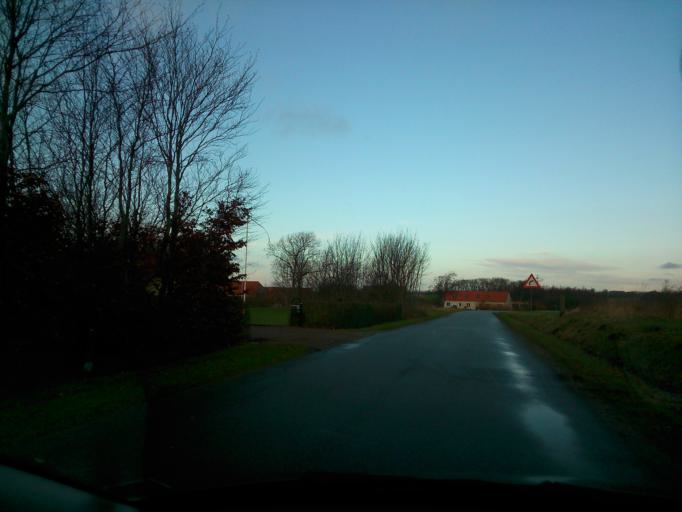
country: DK
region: Central Jutland
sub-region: Ringkobing-Skjern Kommune
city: Skjern
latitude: 56.0255
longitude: 8.5445
